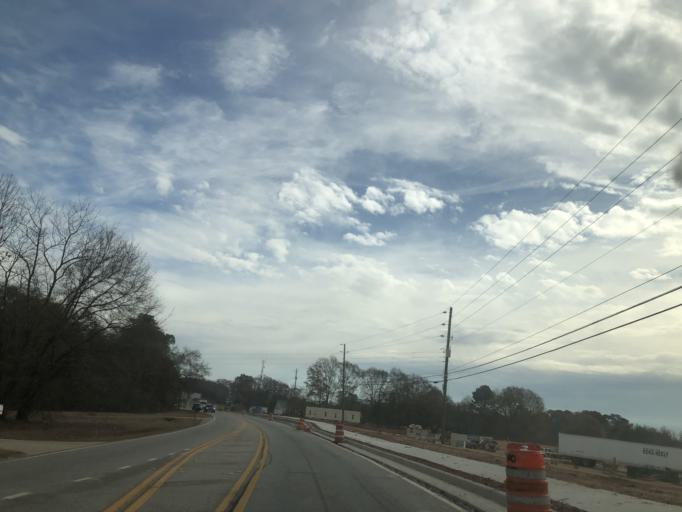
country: US
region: Georgia
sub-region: Henry County
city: Stockbridge
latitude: 33.6095
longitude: -84.2273
